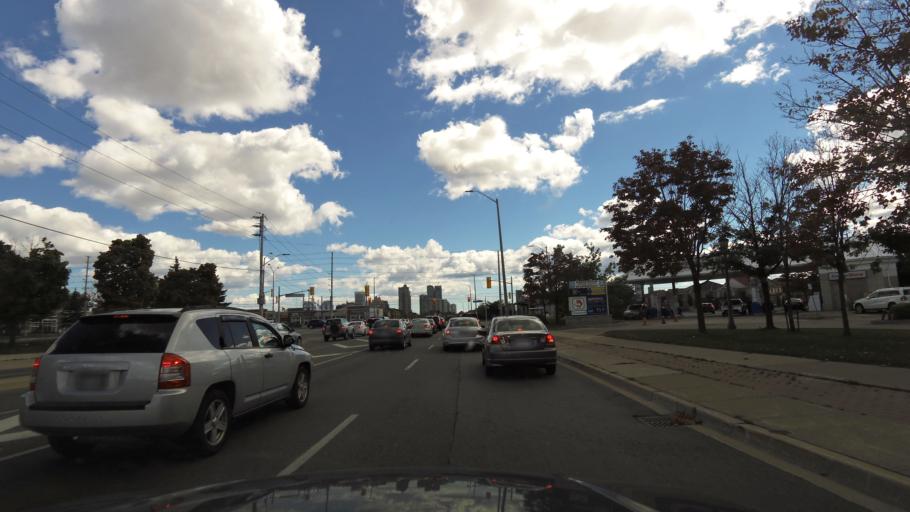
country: CA
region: Ontario
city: Mississauga
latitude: 43.5977
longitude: -79.6644
